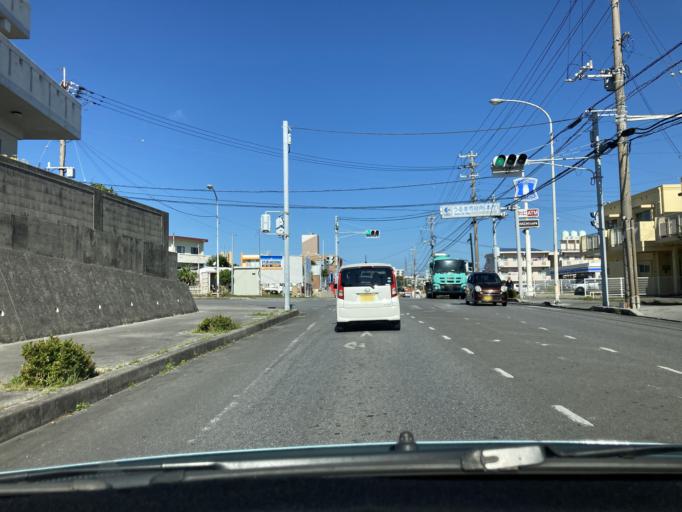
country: JP
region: Okinawa
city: Gushikawa
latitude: 26.3761
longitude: 127.8644
